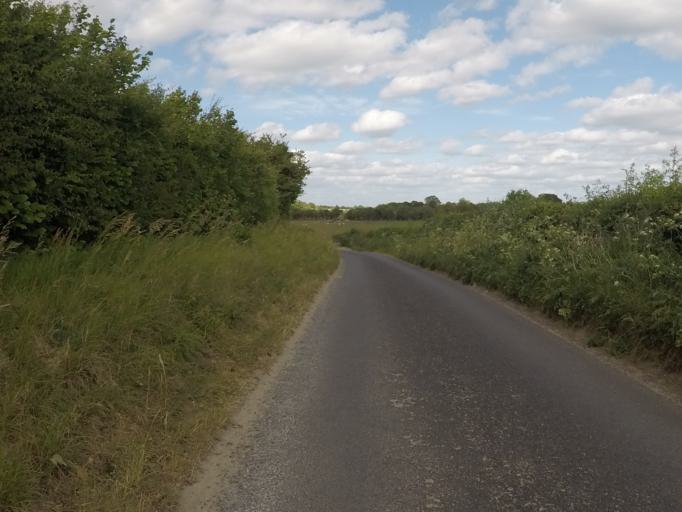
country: GB
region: England
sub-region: Oxfordshire
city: Witney
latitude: 51.8080
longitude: -1.5163
